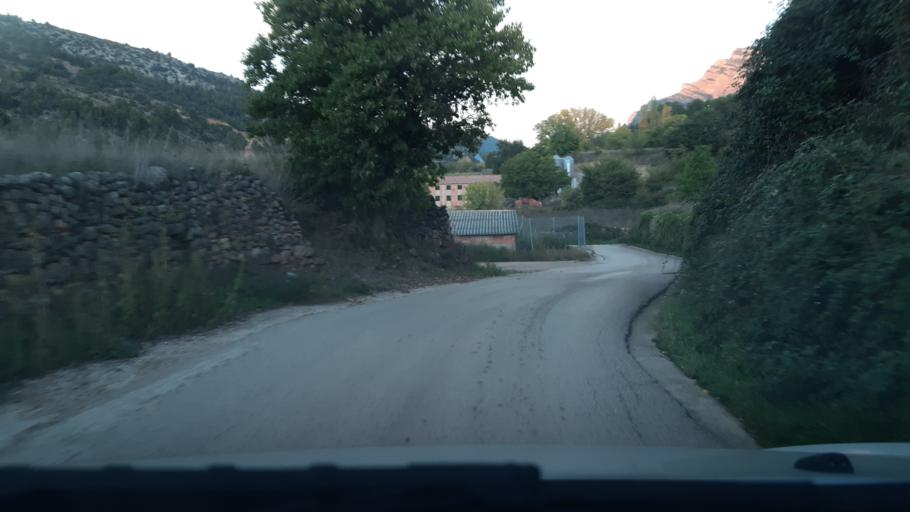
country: ES
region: Aragon
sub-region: Provincia de Teruel
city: Valderrobres
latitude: 40.8376
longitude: 0.1912
